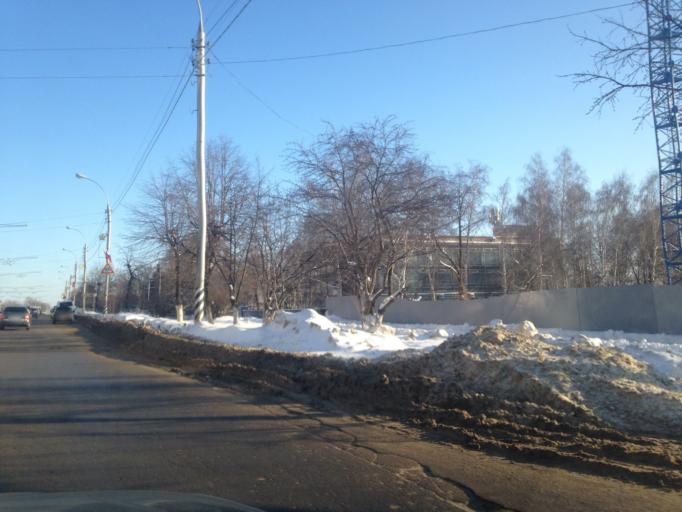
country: RU
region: Ulyanovsk
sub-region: Ulyanovskiy Rayon
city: Ulyanovsk
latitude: 54.3076
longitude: 48.3901
